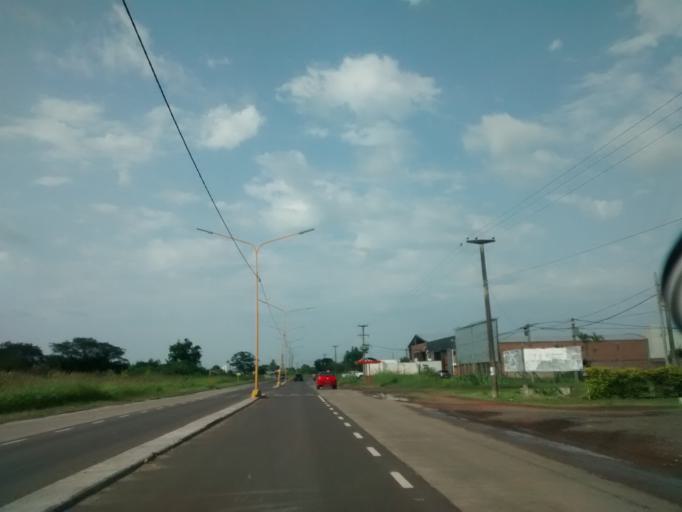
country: AR
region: Chaco
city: Resistencia
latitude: -27.4178
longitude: -58.9714
